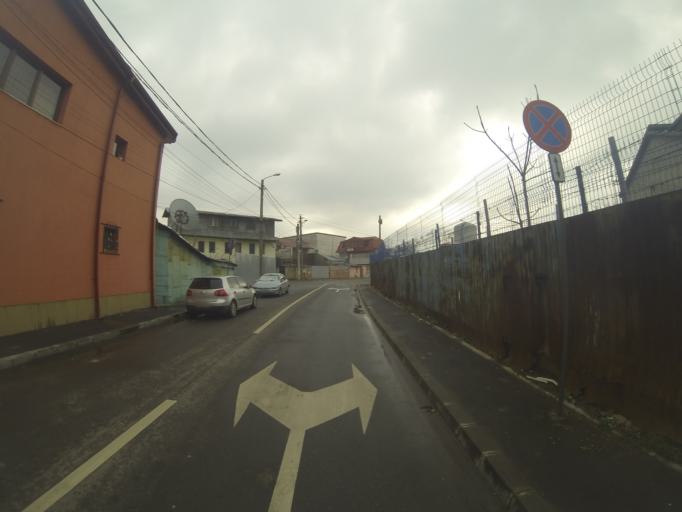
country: RO
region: Bucuresti
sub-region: Municipiul Bucuresti
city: Bucuresti
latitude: 44.4033
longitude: 26.0833
